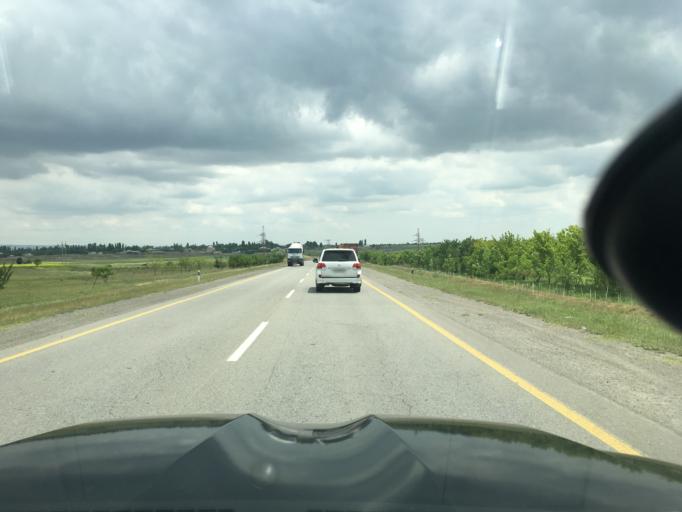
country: AZ
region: Tovuz
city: Qaraxanli
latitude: 41.0295
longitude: 45.6094
